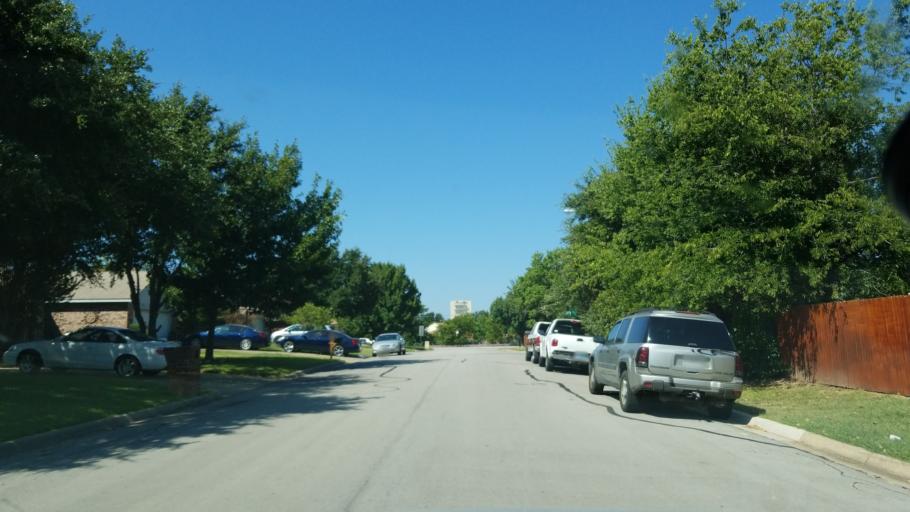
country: US
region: Texas
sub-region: Tarrant County
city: Mansfield
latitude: 32.5537
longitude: -97.1320
